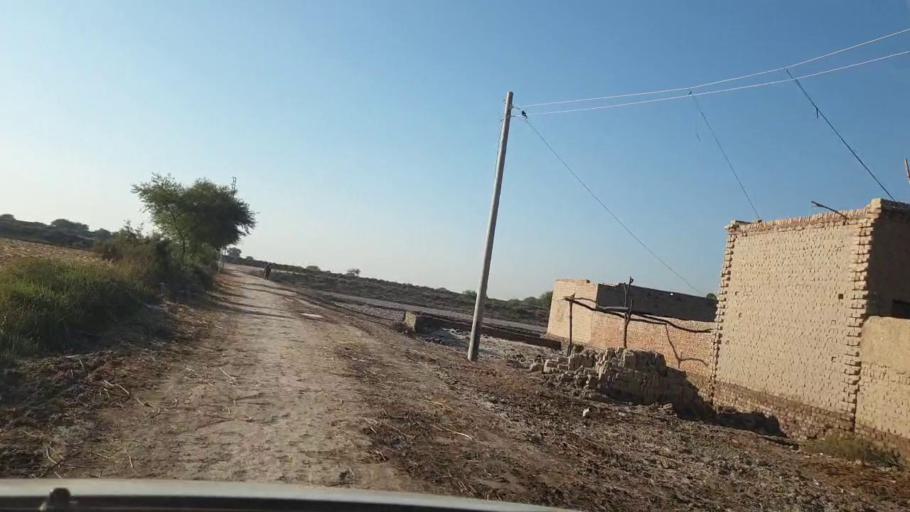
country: PK
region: Sindh
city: Khairpur Nathan Shah
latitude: 27.0356
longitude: 67.7127
